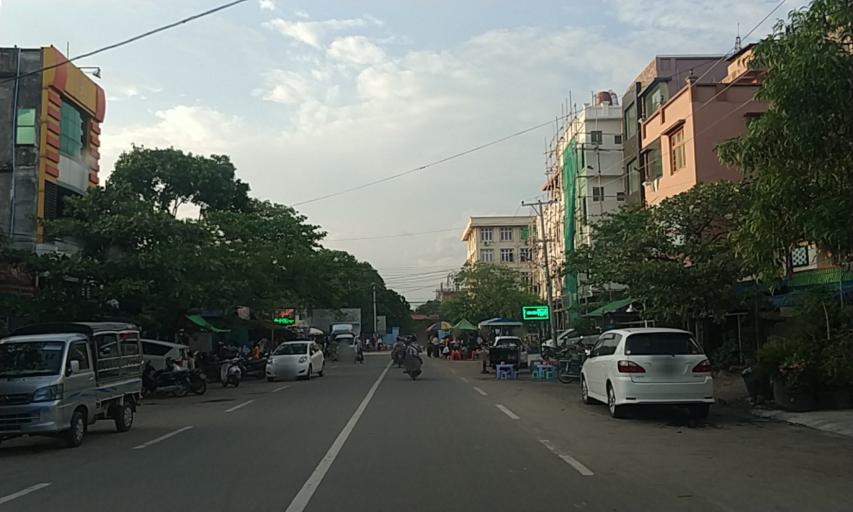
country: MM
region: Mandalay
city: Mandalay
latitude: 21.9759
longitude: 96.0918
